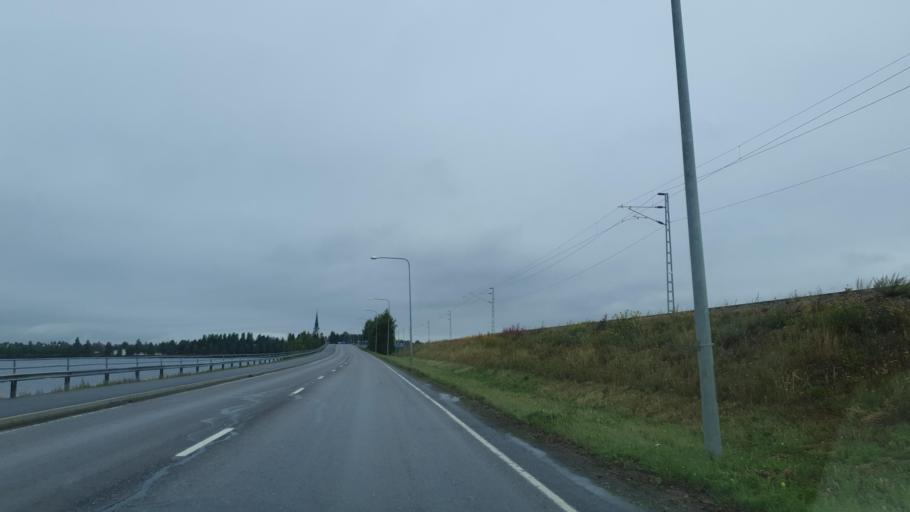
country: FI
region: Lapland
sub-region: Itae-Lappi
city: Kemijaervi
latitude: 66.7159
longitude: 27.4594
